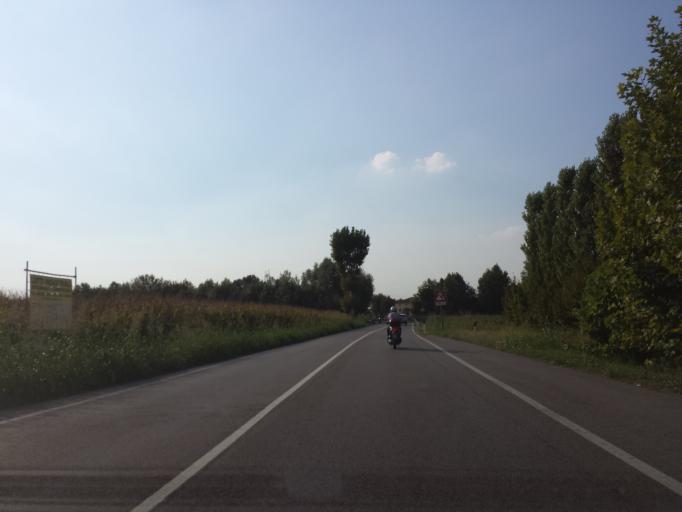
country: IT
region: Veneto
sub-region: Provincia di Vicenza
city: Grumolo delle Abbadesse
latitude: 45.4950
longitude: 11.6595
